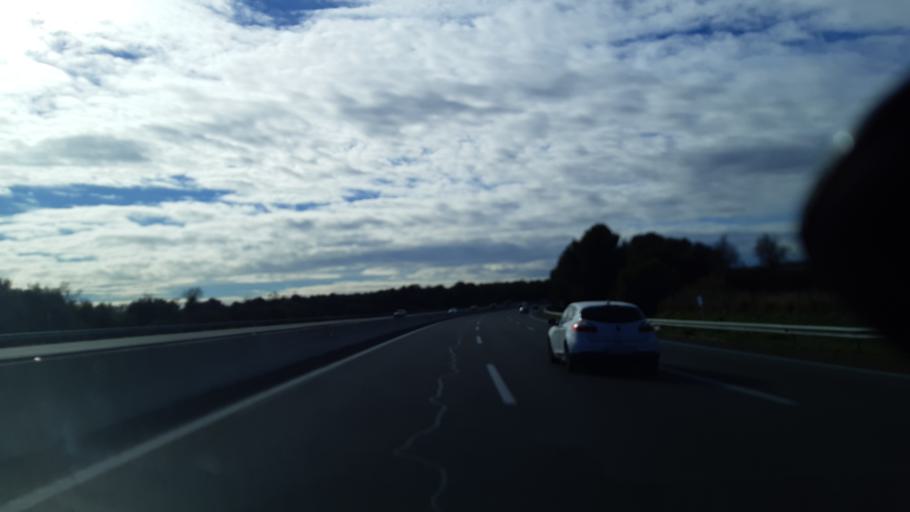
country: ES
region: Catalonia
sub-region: Provincia de Tarragona
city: Sant Jaume dels Domenys
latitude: 41.2947
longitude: 1.5990
